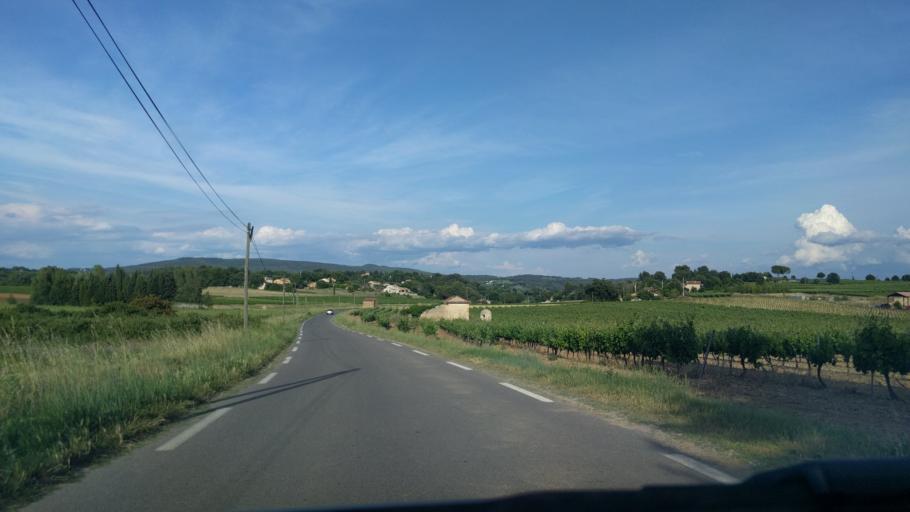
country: FR
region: Provence-Alpes-Cote d'Azur
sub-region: Departement du Vaucluse
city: Pertuis
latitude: 43.7334
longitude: 5.5283
